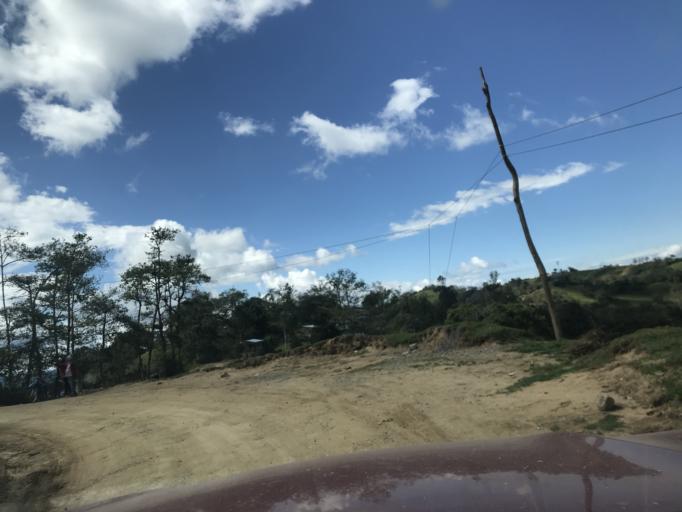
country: PE
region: Cajamarca
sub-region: Provincia de Chota
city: Querocoto
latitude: -6.3427
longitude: -79.0483
